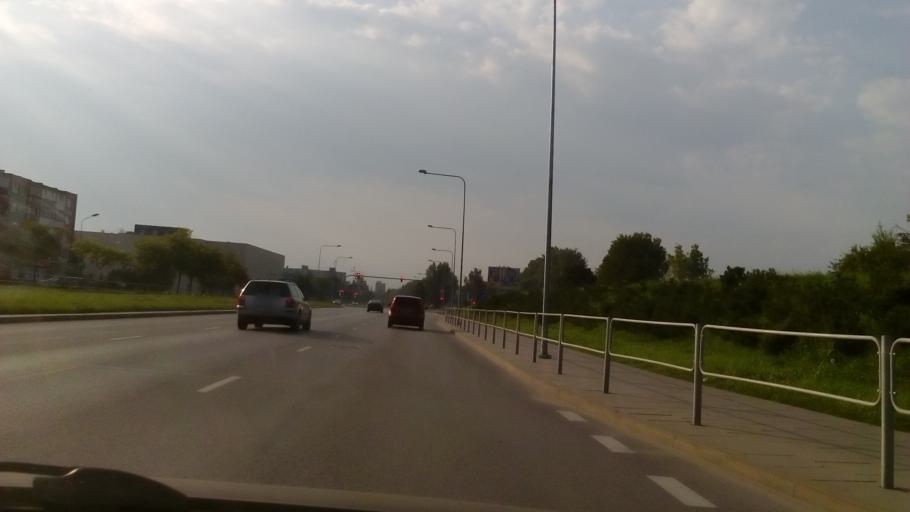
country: LT
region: Alytaus apskritis
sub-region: Alytus
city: Alytus
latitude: 54.4062
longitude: 24.0188
